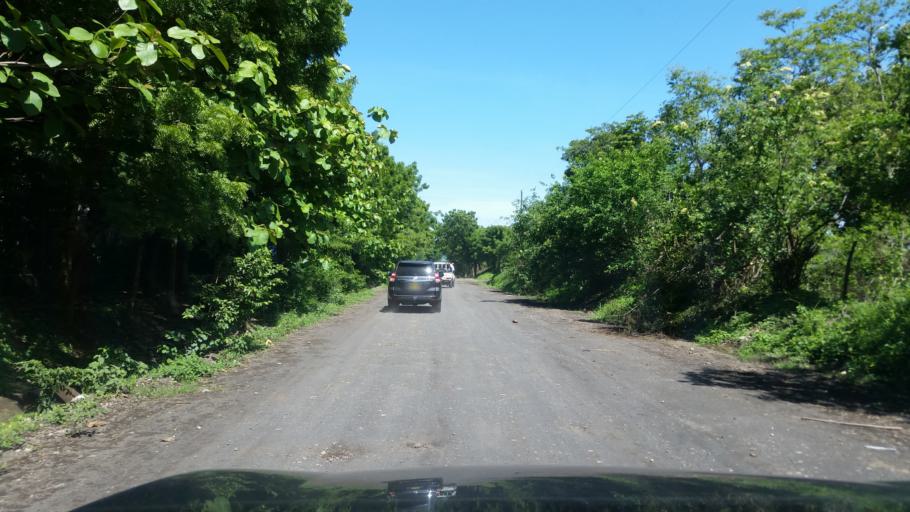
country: NI
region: Chinandega
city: Puerto Morazan
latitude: 12.7695
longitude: -87.0762
